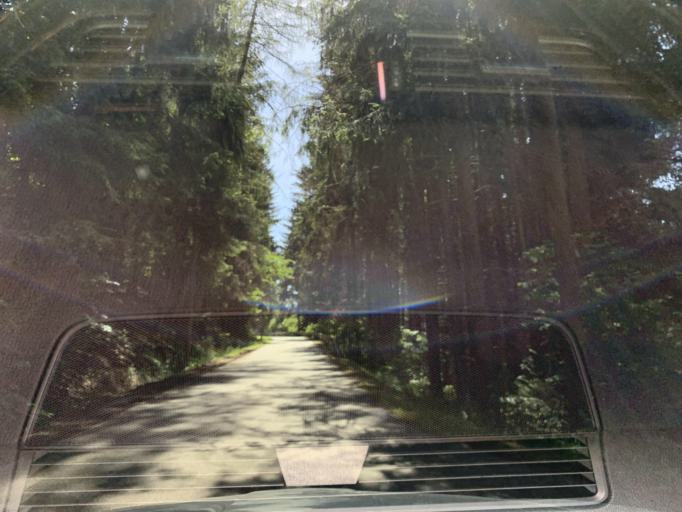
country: DE
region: Bavaria
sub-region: Upper Palatinate
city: Dieterskirchen
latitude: 49.4124
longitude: 12.4195
